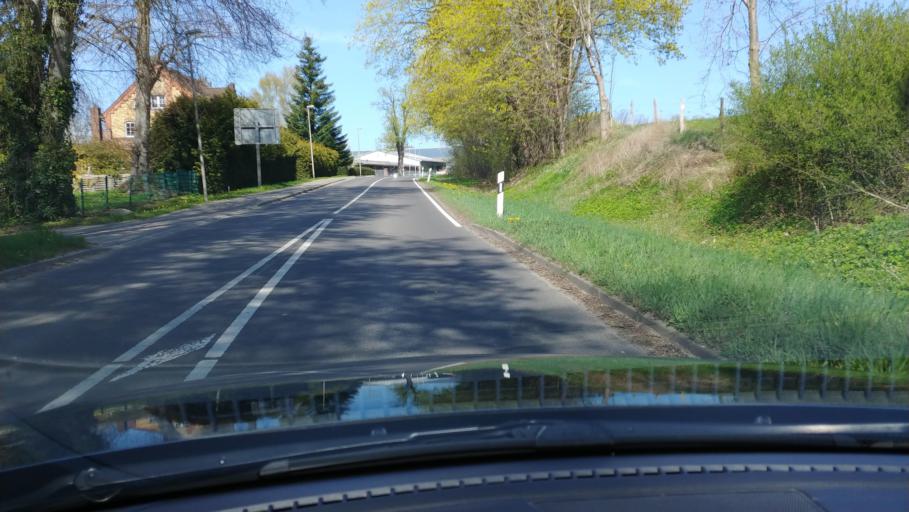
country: DE
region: Mecklenburg-Vorpommern
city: Muhlen Eichsen
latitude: 53.7599
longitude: 11.2520
